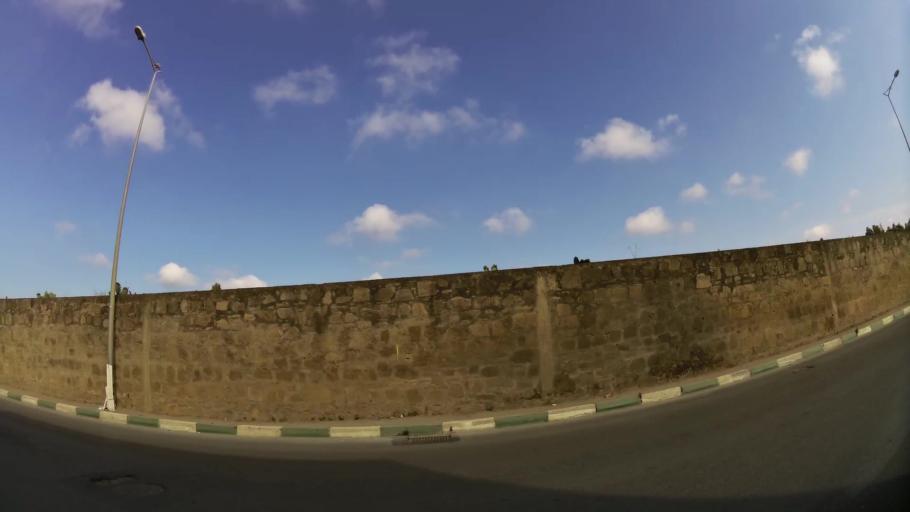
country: MA
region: Rabat-Sale-Zemmour-Zaer
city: Sale
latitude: 34.0578
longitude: -6.7703
